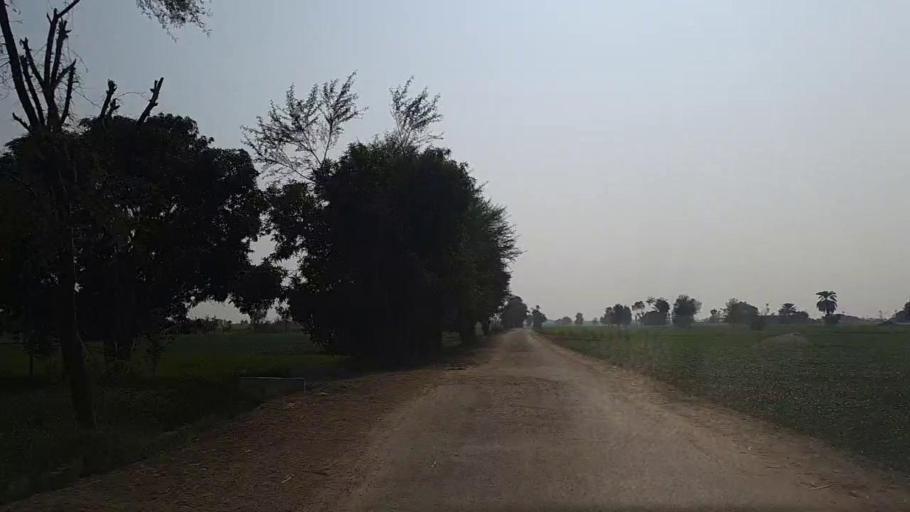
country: PK
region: Sindh
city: Jam Sahib
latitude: 26.4590
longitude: 68.5236
